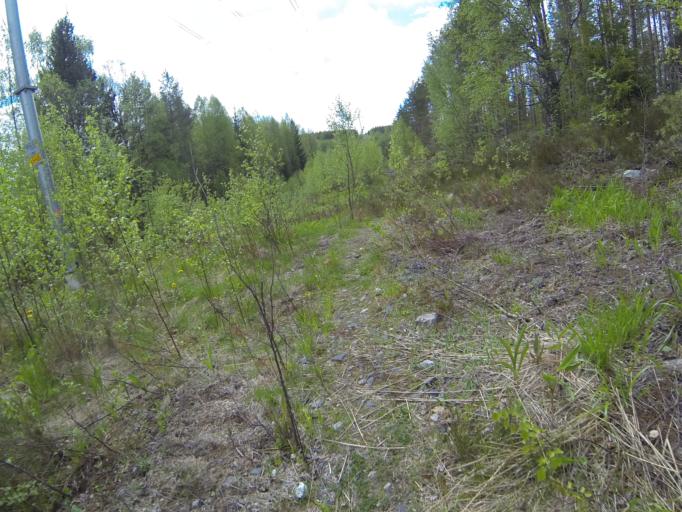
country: FI
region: Varsinais-Suomi
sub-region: Salo
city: Halikko
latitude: 60.3303
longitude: 23.0737
